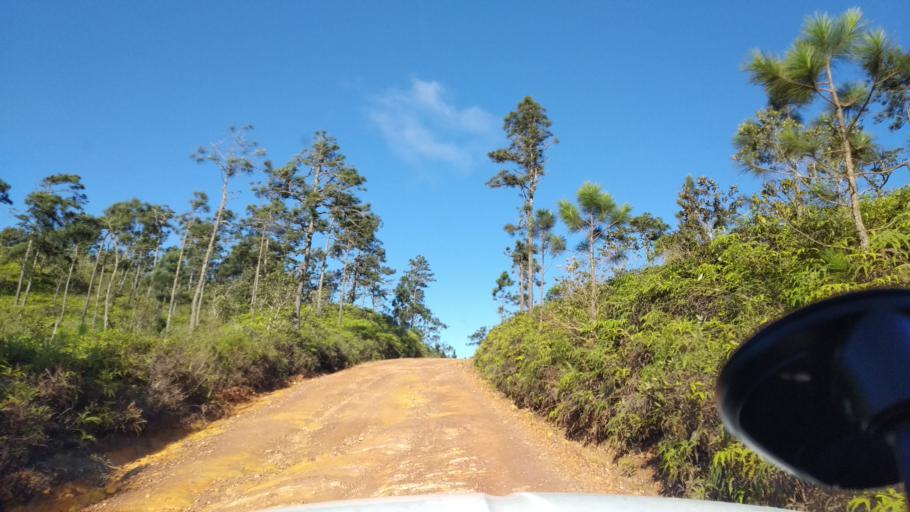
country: BZ
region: Cayo
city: Belmopan
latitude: 16.9990
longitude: -88.8468
